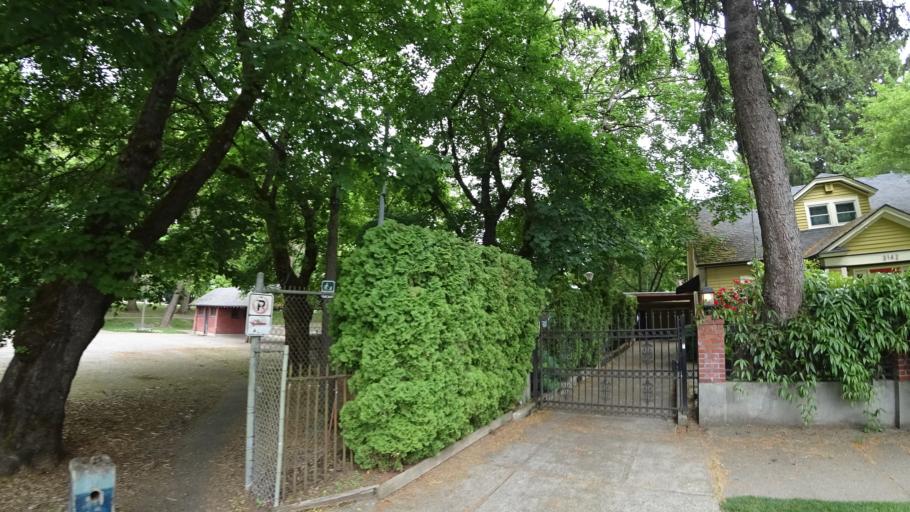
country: US
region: Oregon
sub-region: Multnomah County
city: Portland
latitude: 45.5460
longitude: -122.6575
